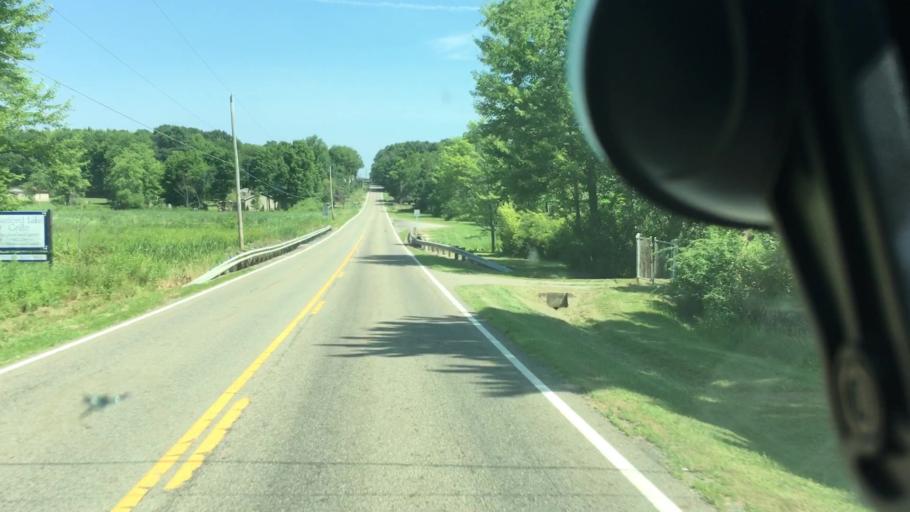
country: US
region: Ohio
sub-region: Columbiana County
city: Lisbon
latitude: 40.7956
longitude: -80.8586
